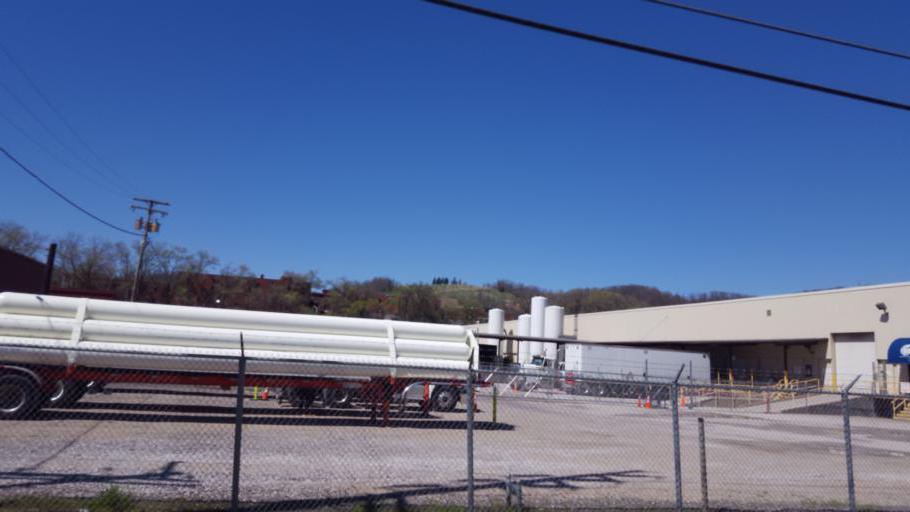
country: US
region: Ohio
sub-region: Belmont County
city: Martins Ferry
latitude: 40.0964
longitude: -80.7183
